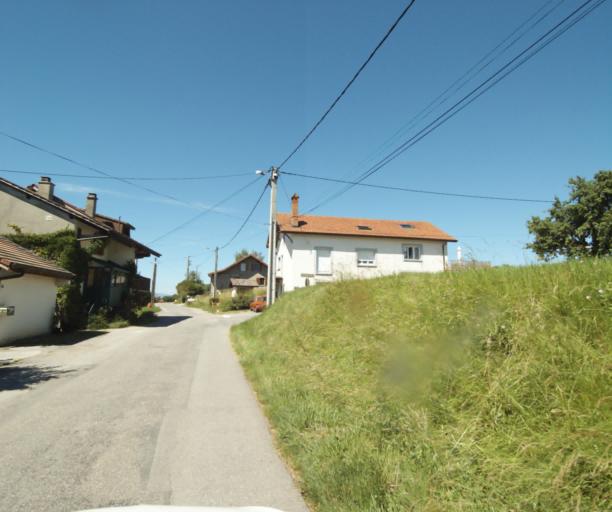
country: FR
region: Rhone-Alpes
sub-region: Departement de la Haute-Savoie
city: Ballaison
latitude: 46.2862
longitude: 6.3251
